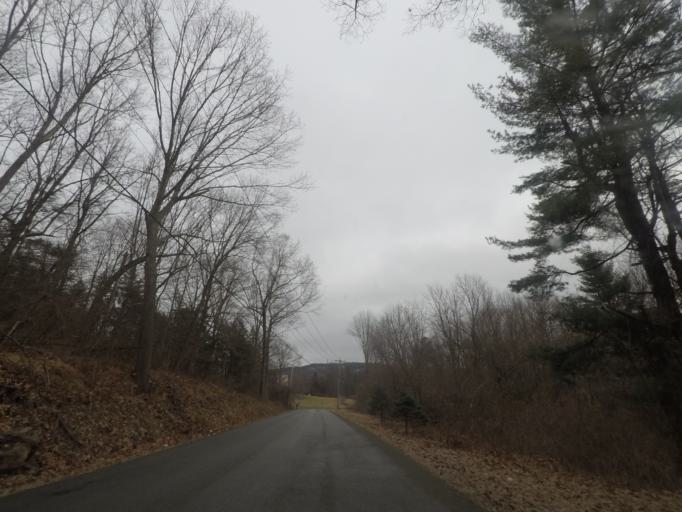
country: US
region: New York
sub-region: Saratoga County
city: Waterford
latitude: 42.7705
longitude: -73.6457
